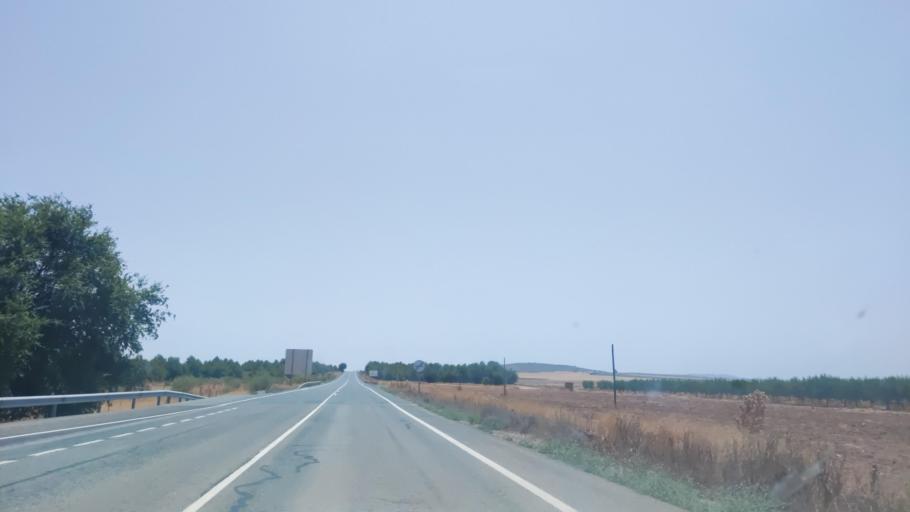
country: ES
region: Castille-La Mancha
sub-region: Provincia de Albacete
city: Pozo-Canada
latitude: 38.8518
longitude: -1.7684
